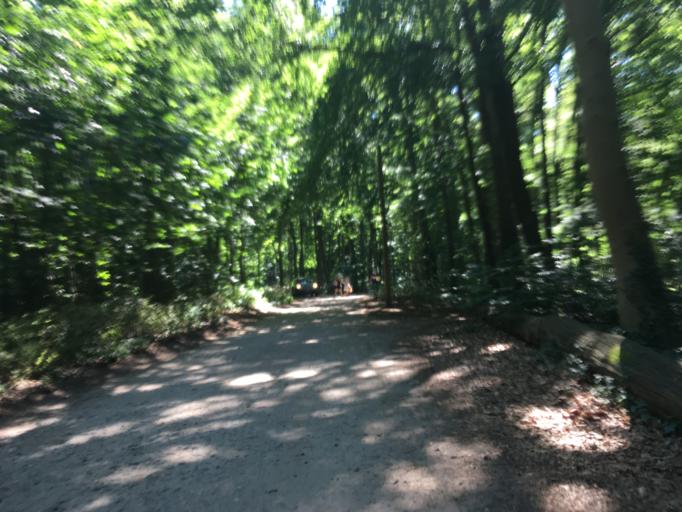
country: DE
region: Brandenburg
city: Grosswoltersdorf
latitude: 53.1508
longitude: 13.0424
